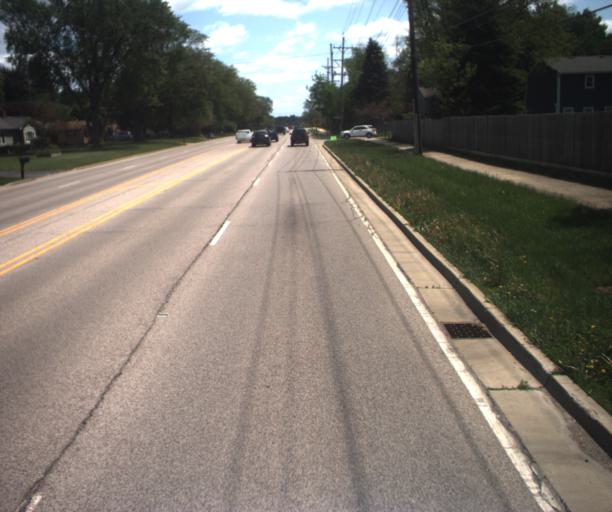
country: US
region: Illinois
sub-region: Kane County
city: Batavia
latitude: 41.8640
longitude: -88.3215
